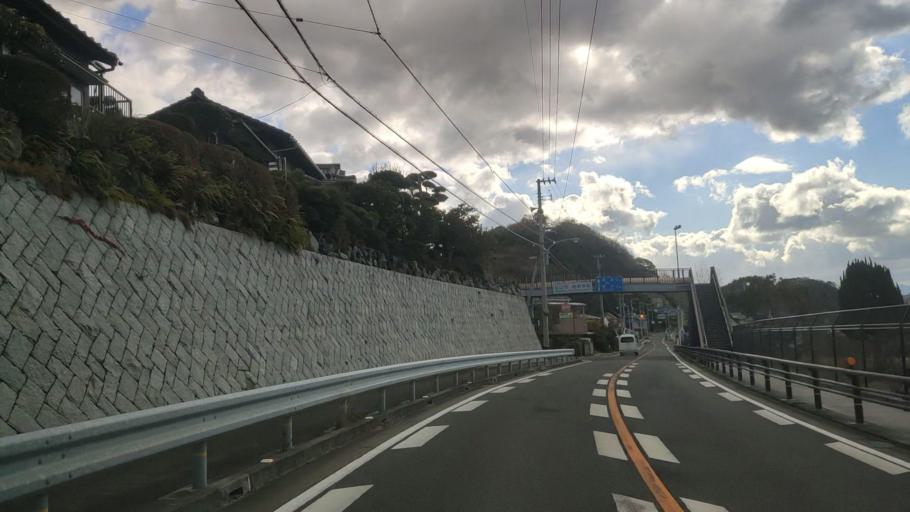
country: JP
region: Ehime
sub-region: Shikoku-chuo Shi
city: Matsuyama
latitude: 33.8763
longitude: 132.7072
